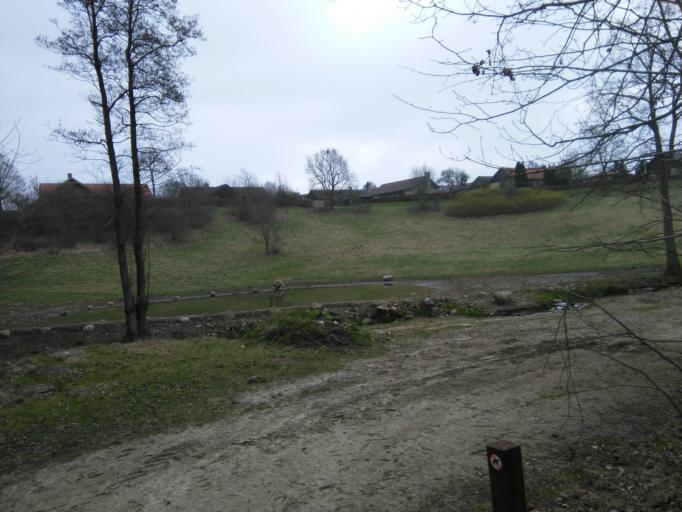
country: DK
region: Central Jutland
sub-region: Arhus Kommune
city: Beder
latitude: 56.0661
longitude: 10.2081
